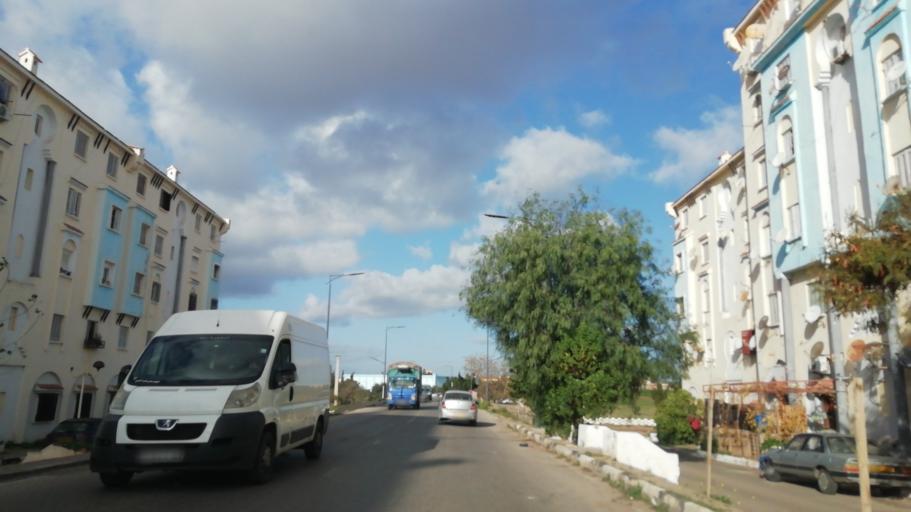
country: DZ
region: Ain Temouchent
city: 'Ain Temouchent
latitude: 35.3024
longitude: -1.1553
